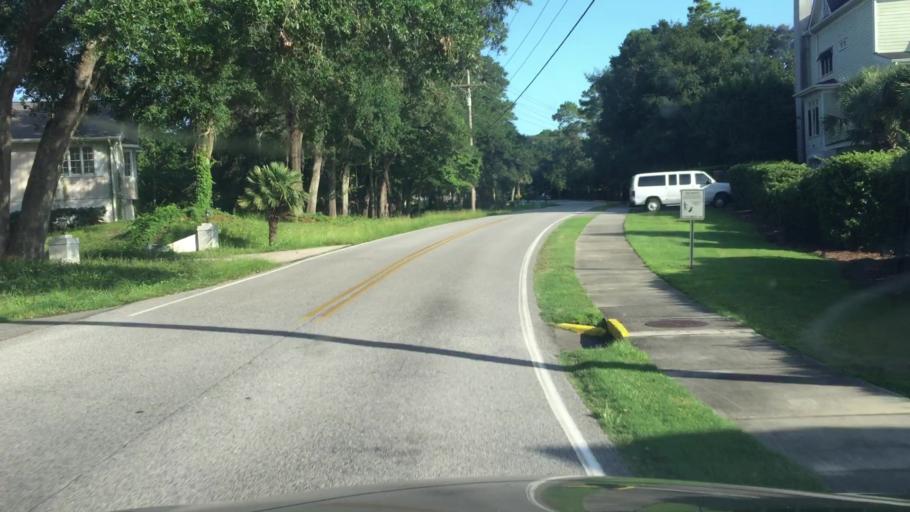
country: US
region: South Carolina
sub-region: Horry County
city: North Myrtle Beach
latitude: 33.8275
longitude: -78.6661
